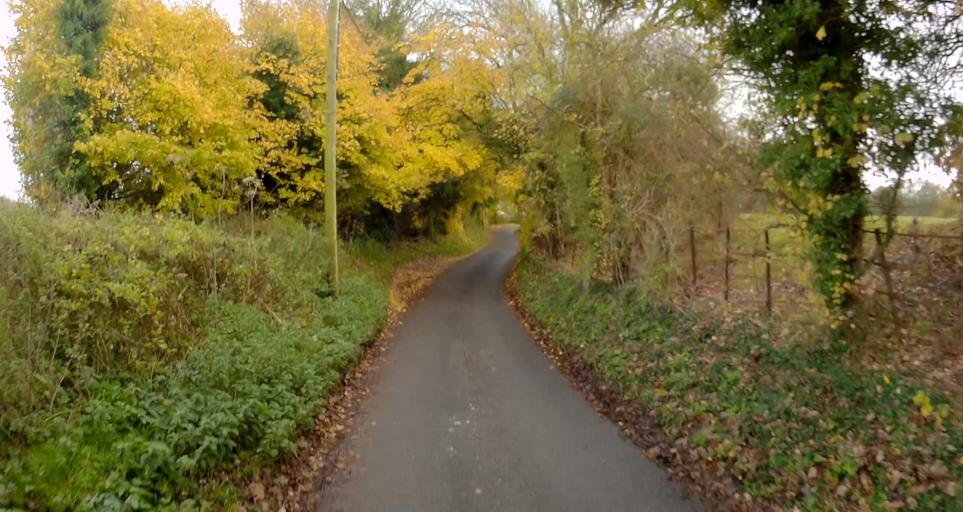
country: GB
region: England
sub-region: Hampshire
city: Long Sutton
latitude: 51.2196
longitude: -0.9649
